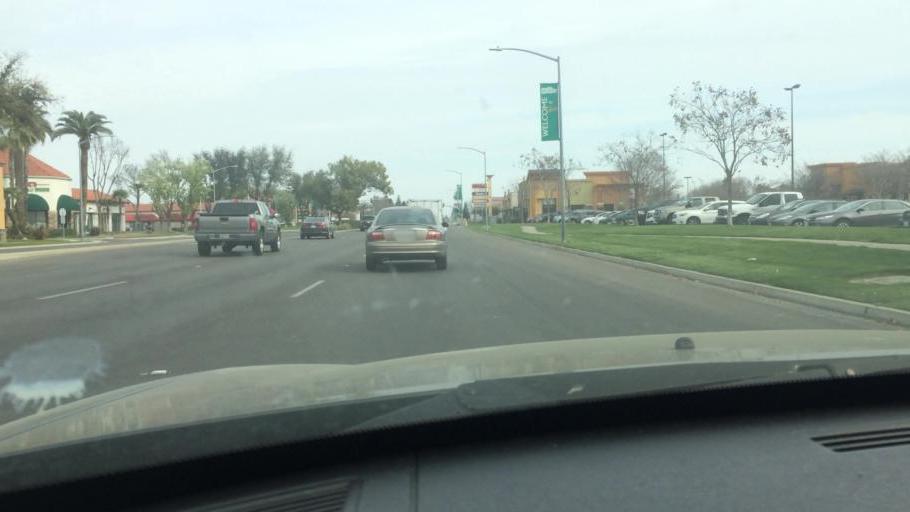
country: US
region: California
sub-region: Fresno County
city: Tarpey Village
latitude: 36.8085
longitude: -119.6937
